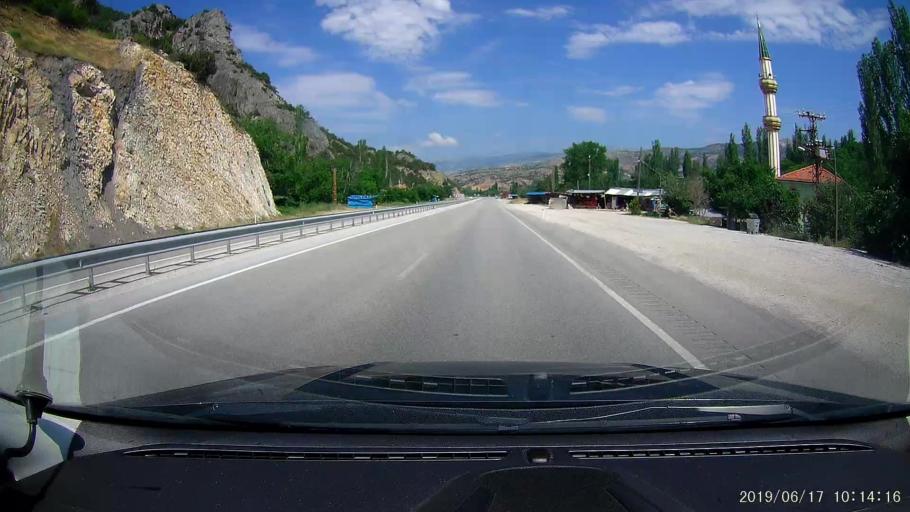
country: TR
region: Amasya
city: Saraycik
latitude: 40.9888
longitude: 35.0297
